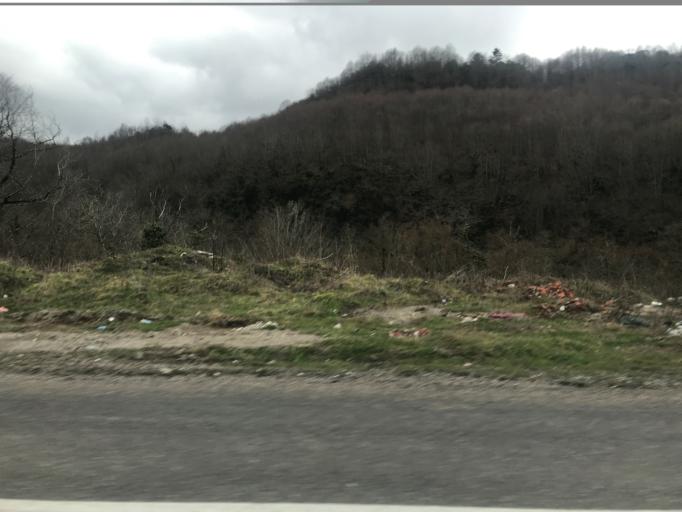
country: TR
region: Bartin
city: Amasra
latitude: 41.6978
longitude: 32.3841
